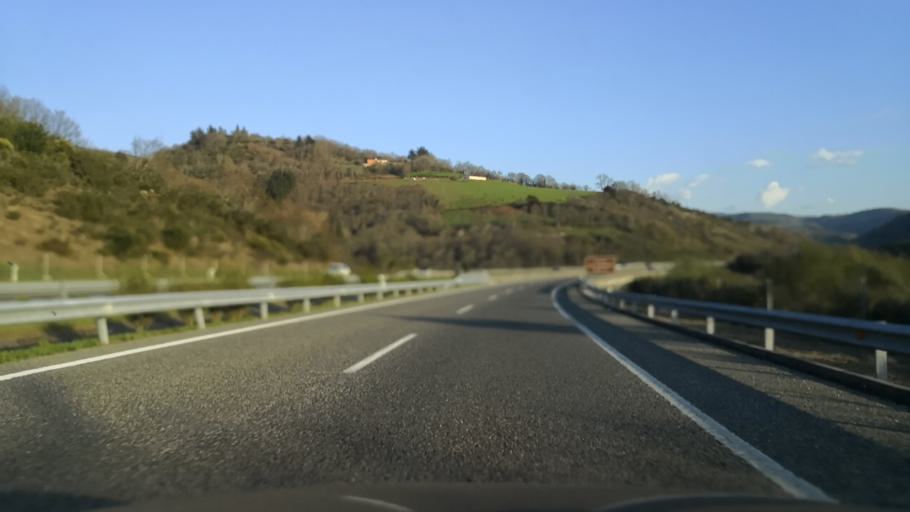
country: ES
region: Galicia
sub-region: Provincia de Lugo
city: Becerrea
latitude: 42.8201
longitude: -7.1099
